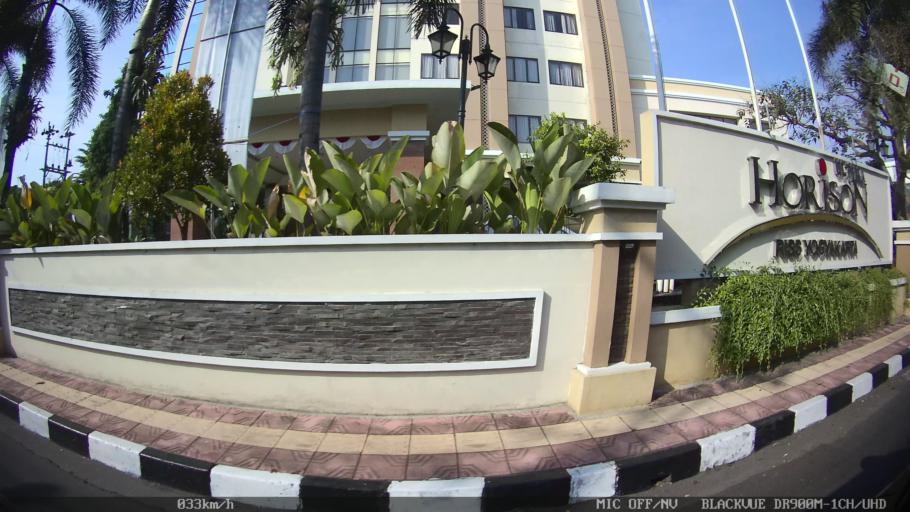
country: ID
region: Daerah Istimewa Yogyakarta
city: Yogyakarta
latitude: -7.7874
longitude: 110.3644
